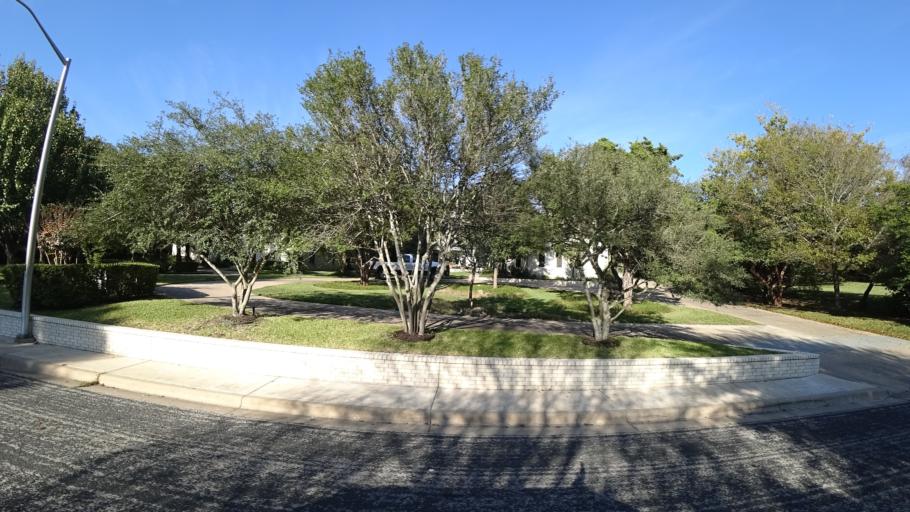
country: US
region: Texas
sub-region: Williamson County
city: Anderson Mill
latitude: 30.4399
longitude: -97.8117
